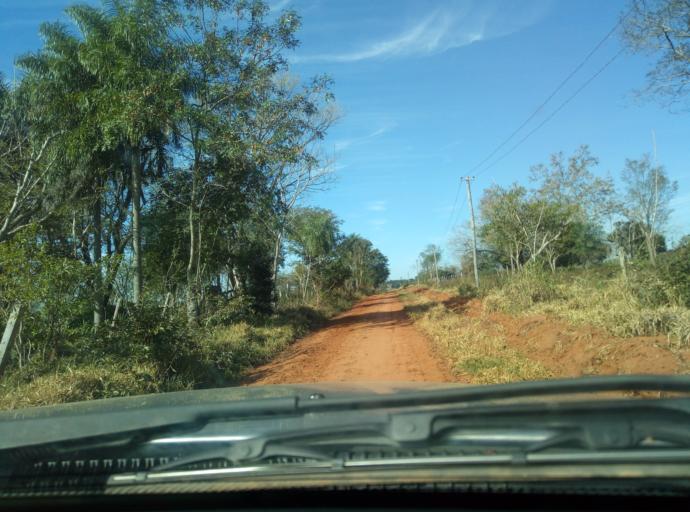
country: PY
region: Caaguazu
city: Carayao
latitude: -25.1706
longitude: -56.2968
